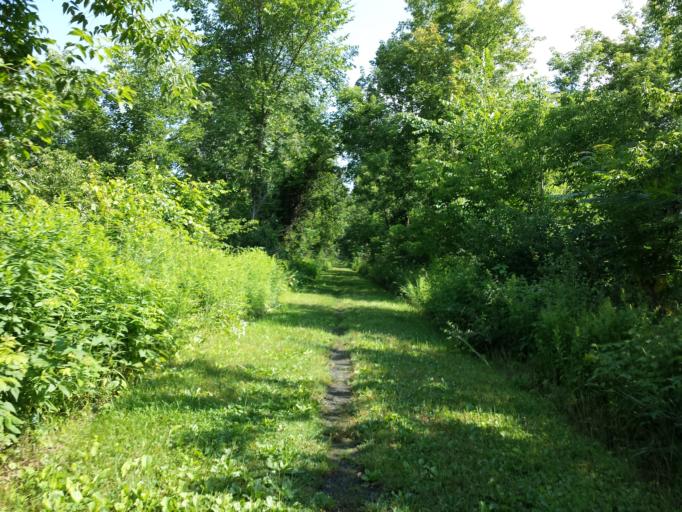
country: US
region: Vermont
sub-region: Rutland County
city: Poultney
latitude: 43.5077
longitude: -73.2380
